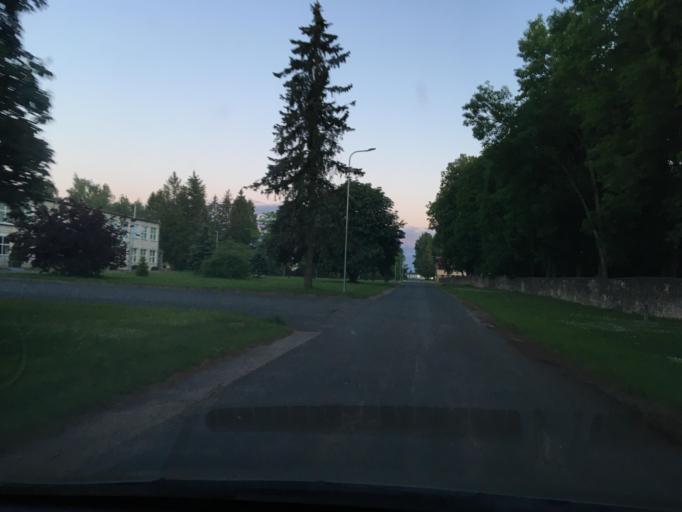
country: EE
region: Jaervamaa
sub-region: Jaerva-Jaani vald
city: Jarva-Jaani
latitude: 59.0305
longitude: 25.7078
